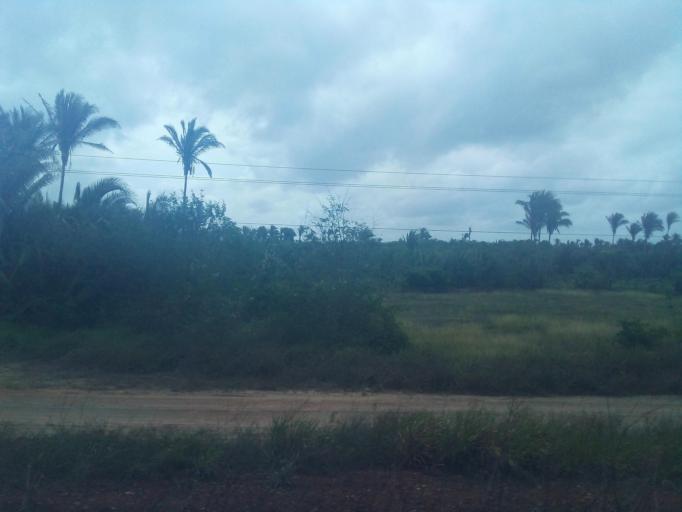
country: BR
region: Maranhao
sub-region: Itapecuru Mirim
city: Itapecuru Mirim
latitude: -3.1860
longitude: -44.3738
